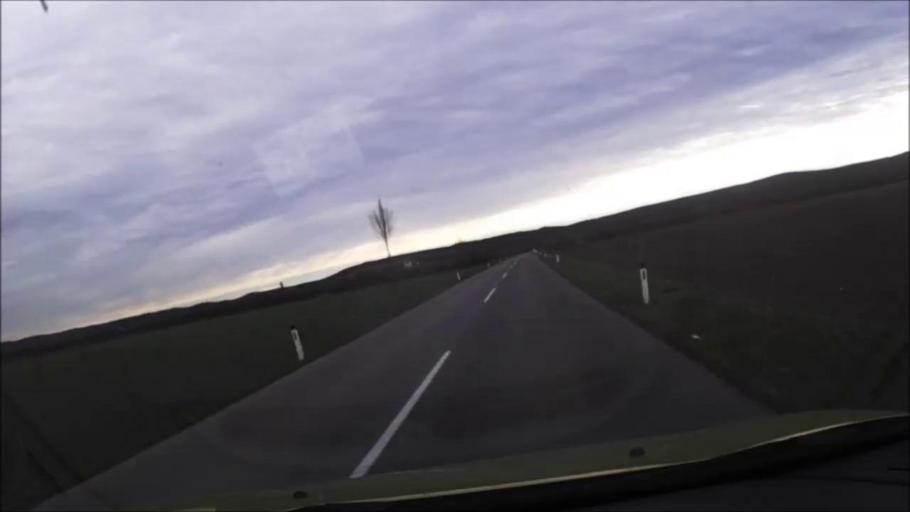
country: AT
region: Burgenland
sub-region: Eisenstadt-Umgebung
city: Leithaprodersdorf
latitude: 47.9278
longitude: 16.4984
